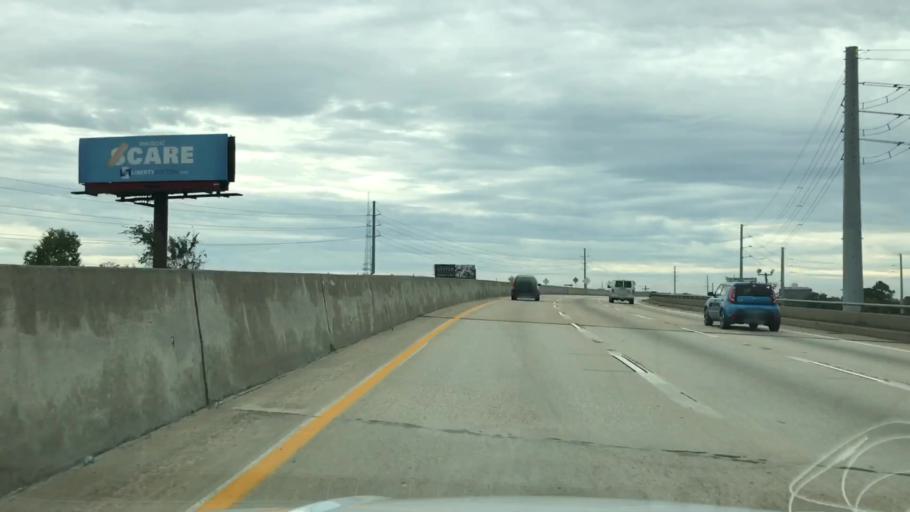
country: US
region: South Carolina
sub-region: Charleston County
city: North Charleston
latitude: 32.8266
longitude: -79.9542
